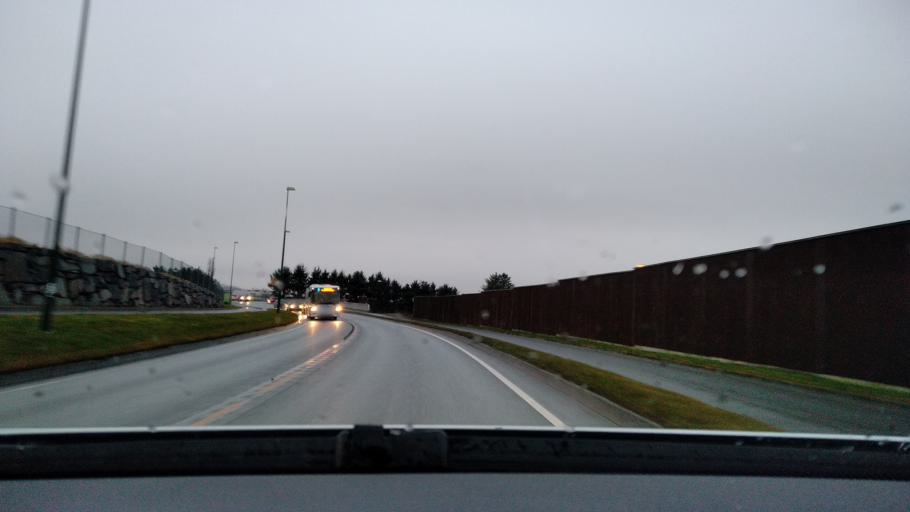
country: NO
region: Rogaland
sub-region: Randaberg
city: Randaberg
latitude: 58.9546
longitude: 5.6382
